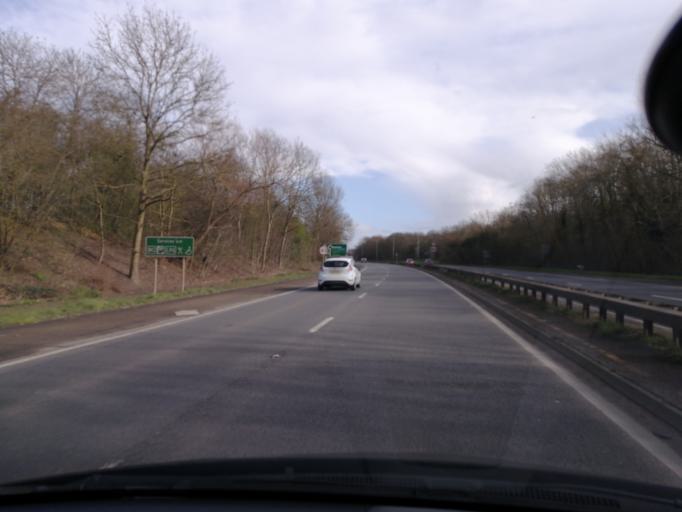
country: GB
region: England
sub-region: Peterborough
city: Eye
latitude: 52.5989
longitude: -0.2167
